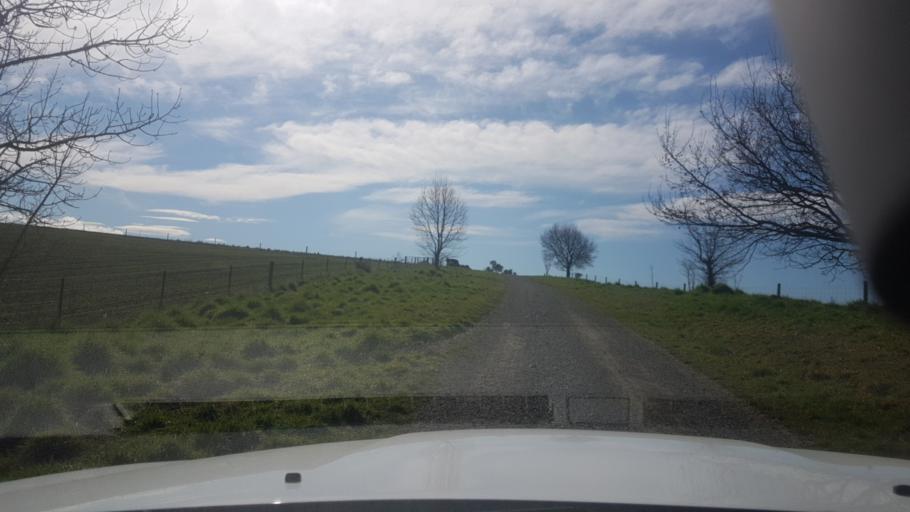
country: NZ
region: Canterbury
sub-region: Timaru District
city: Pleasant Point
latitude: -44.1994
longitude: 171.1873
